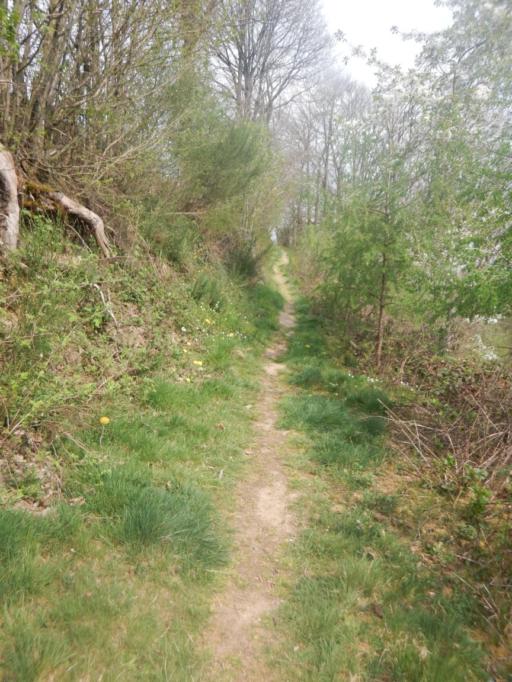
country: LU
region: Diekirch
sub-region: Canton de Wiltz
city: Esch-sur-Sure
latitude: 49.9186
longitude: 5.9162
